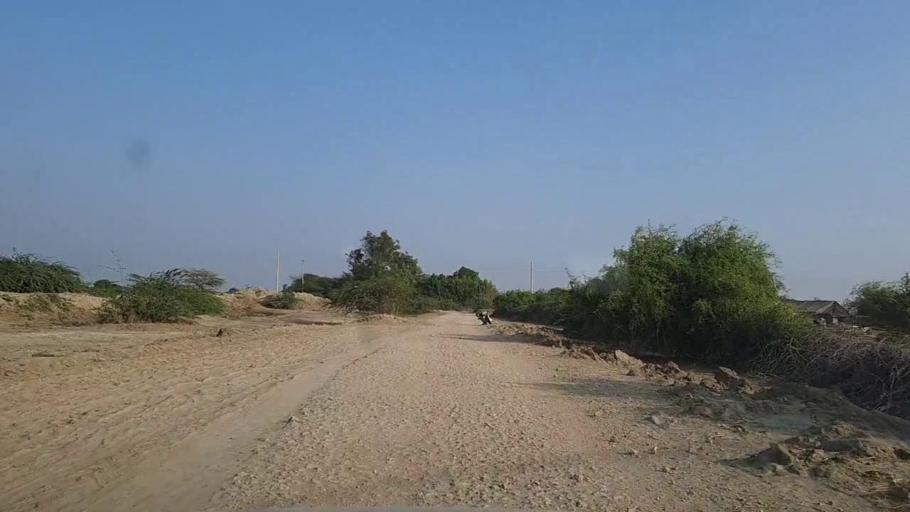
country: PK
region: Sindh
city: Mirpur Sakro
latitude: 24.5993
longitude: 67.6572
